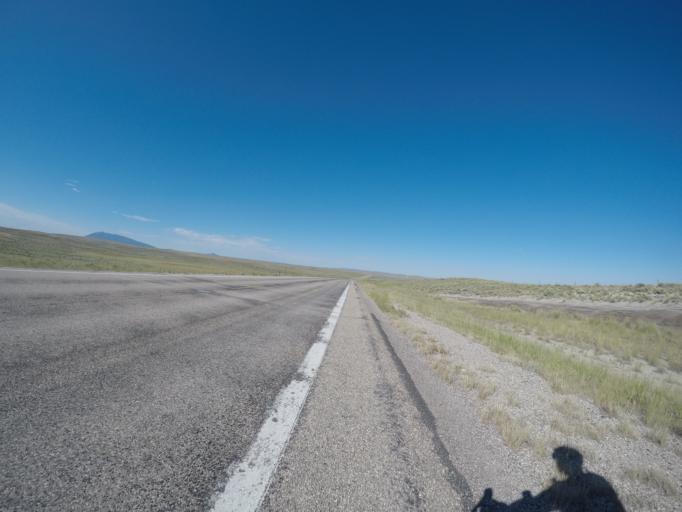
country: US
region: Wyoming
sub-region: Carbon County
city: Saratoga
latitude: 41.8761
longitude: -106.4922
